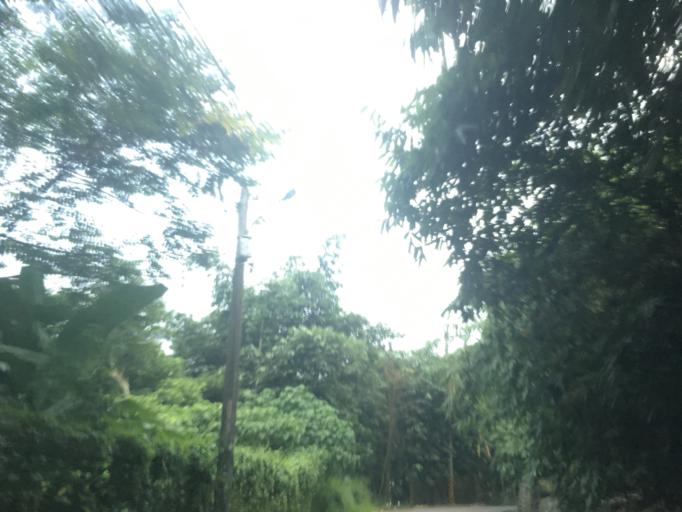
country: TW
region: Taiwan
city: Fengyuan
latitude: 24.1880
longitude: 120.7468
